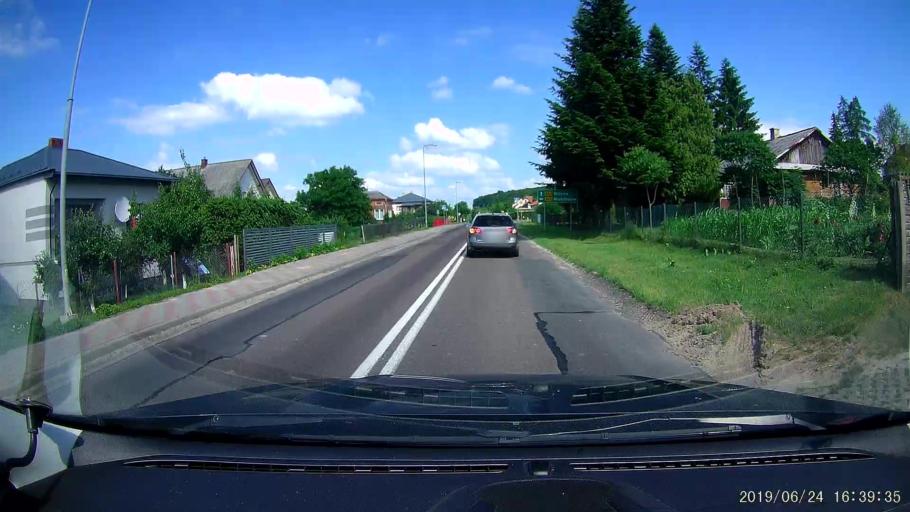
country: PL
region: Lublin Voivodeship
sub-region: Powiat tomaszowski
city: Rachanie
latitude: 50.5297
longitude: 23.5572
